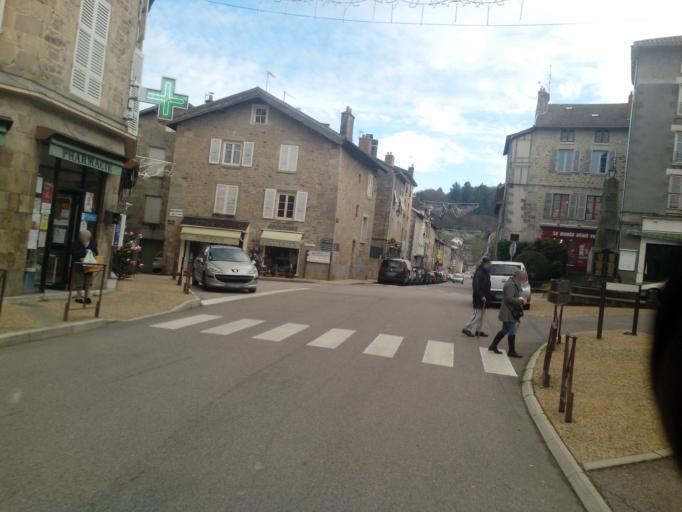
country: FR
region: Limousin
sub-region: Departement de la Haute-Vienne
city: Eymoutiers
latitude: 45.7390
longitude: 1.7431
